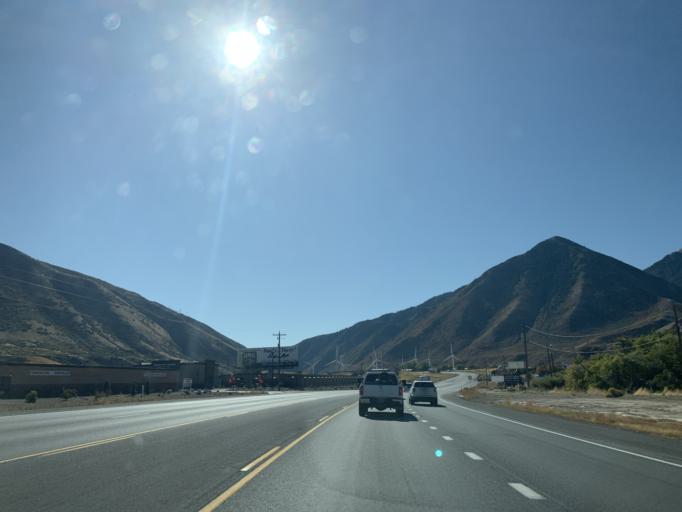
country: US
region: Utah
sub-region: Utah County
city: Mapleton
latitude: 40.0894
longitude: -111.5963
